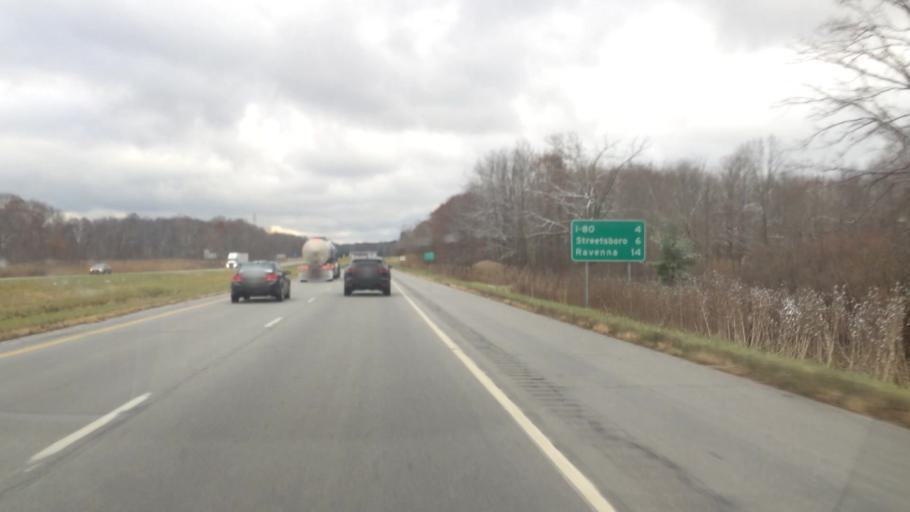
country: US
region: Ohio
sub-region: Summit County
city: Twinsburg
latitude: 41.2979
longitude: -81.4280
